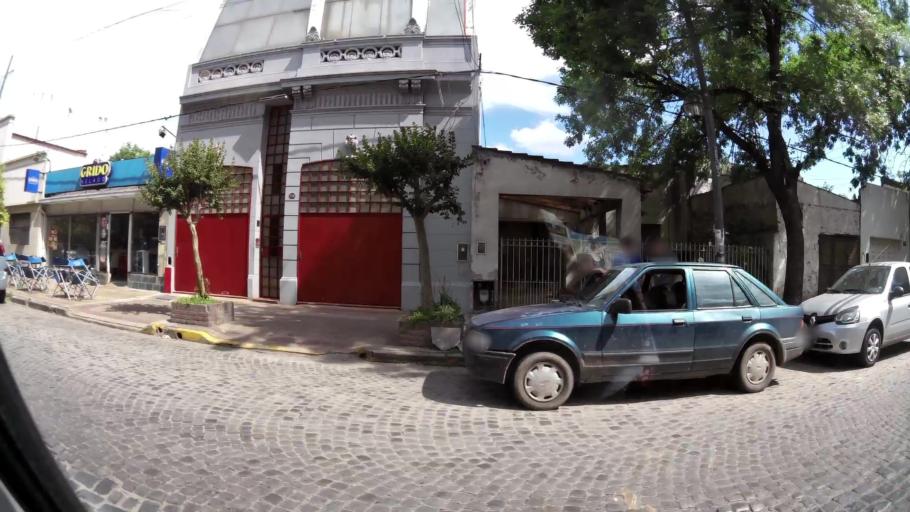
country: AR
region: Buenos Aires
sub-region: Partido de La Plata
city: La Plata
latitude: -34.9209
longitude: -57.9286
